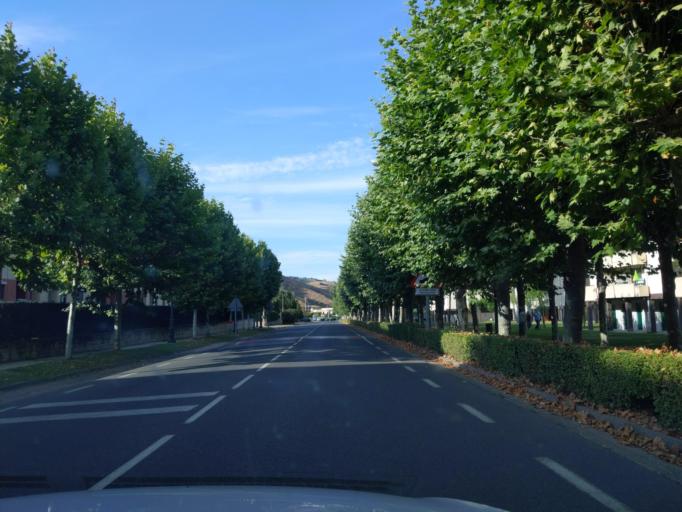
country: ES
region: La Rioja
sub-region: Provincia de La Rioja
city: Ezcaray
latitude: 42.3300
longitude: -3.0135
